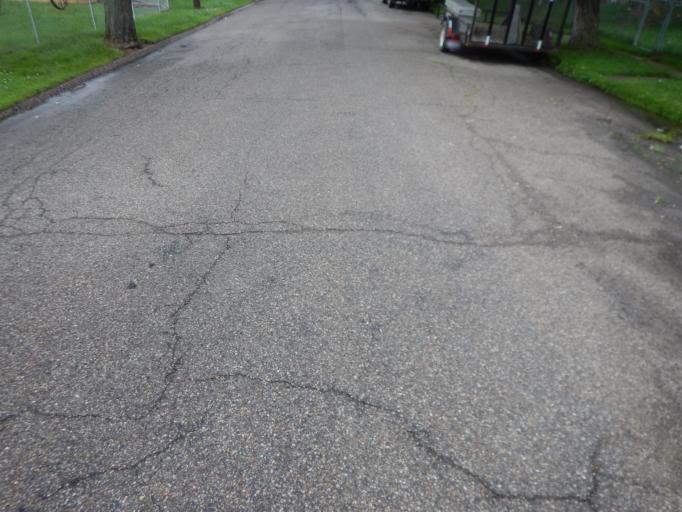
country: US
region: Ohio
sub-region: Muskingum County
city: North Zanesville
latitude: 39.9629
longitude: -82.0147
